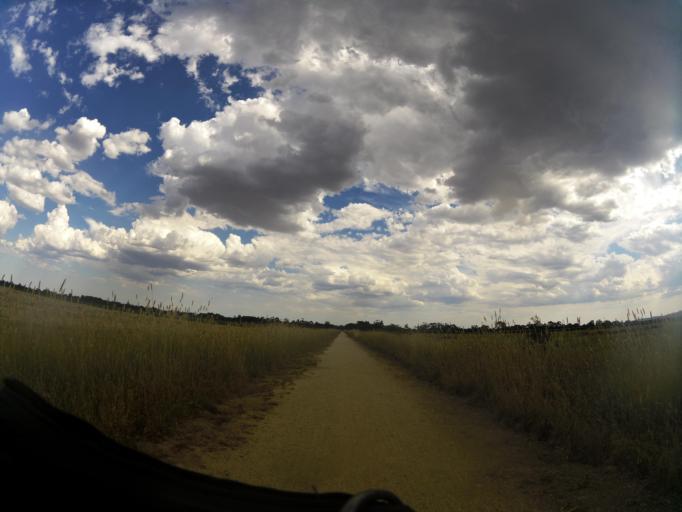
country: AU
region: Victoria
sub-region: Wellington
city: Heyfield
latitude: -38.0018
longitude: 146.6980
